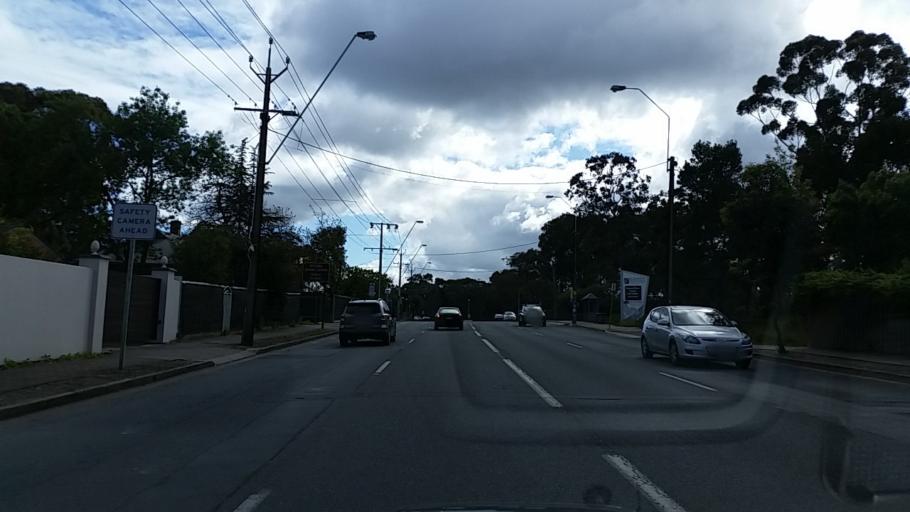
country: AU
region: South Australia
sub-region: Mitcham
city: Blackwood
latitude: -35.0242
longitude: 138.6062
